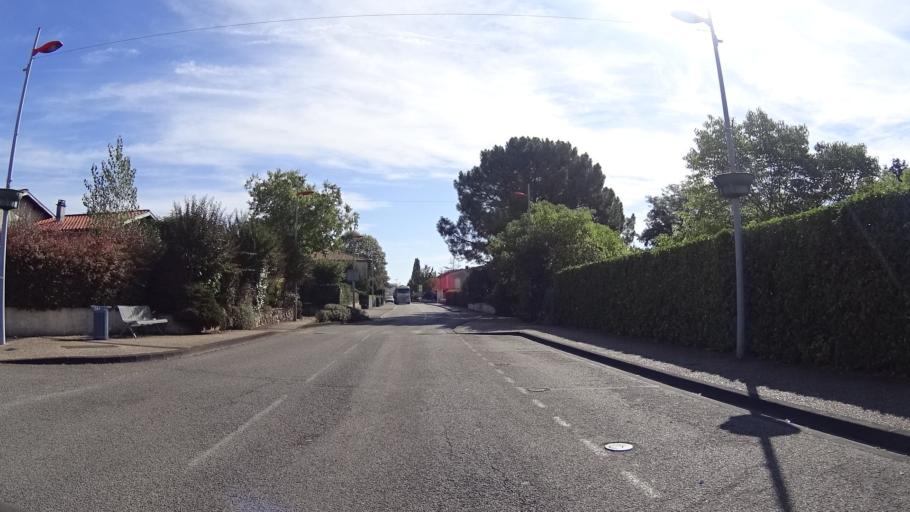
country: FR
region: Aquitaine
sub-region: Departement du Lot-et-Garonne
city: Bon-Encontre
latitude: 44.1869
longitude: 0.6655
